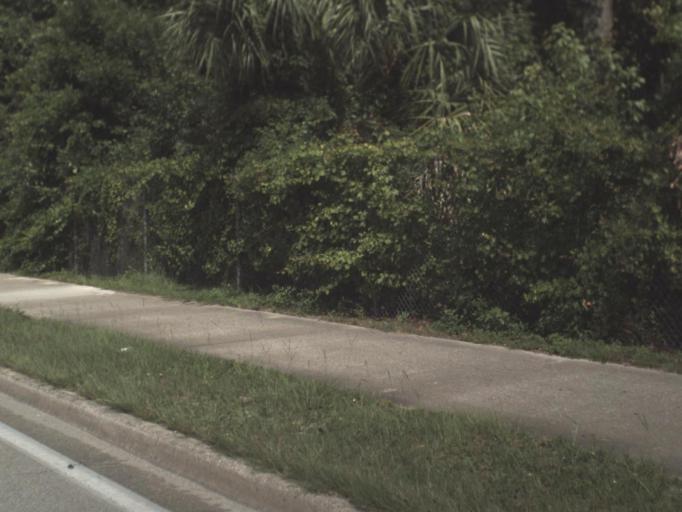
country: US
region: Florida
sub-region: Alachua County
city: Gainesville
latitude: 29.6307
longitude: -82.3653
